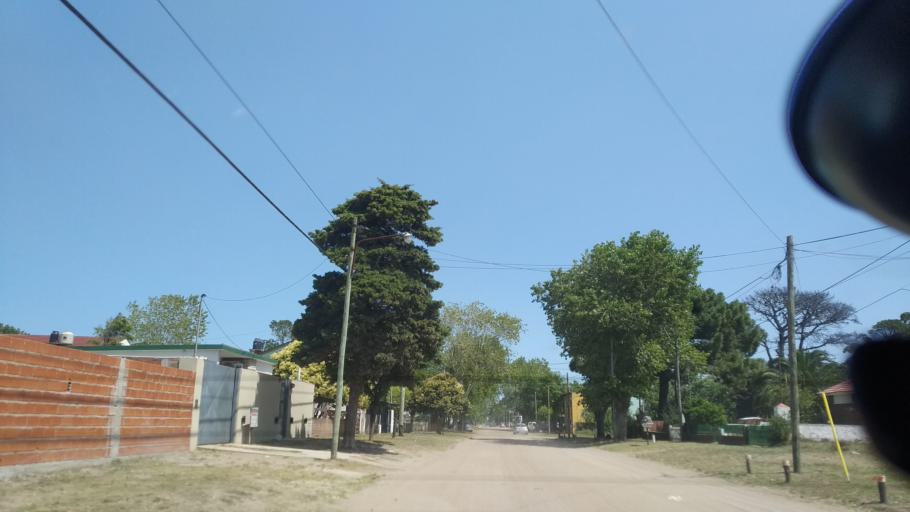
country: AR
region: Buenos Aires
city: Mar del Tuyu
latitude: -36.5683
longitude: -56.6942
